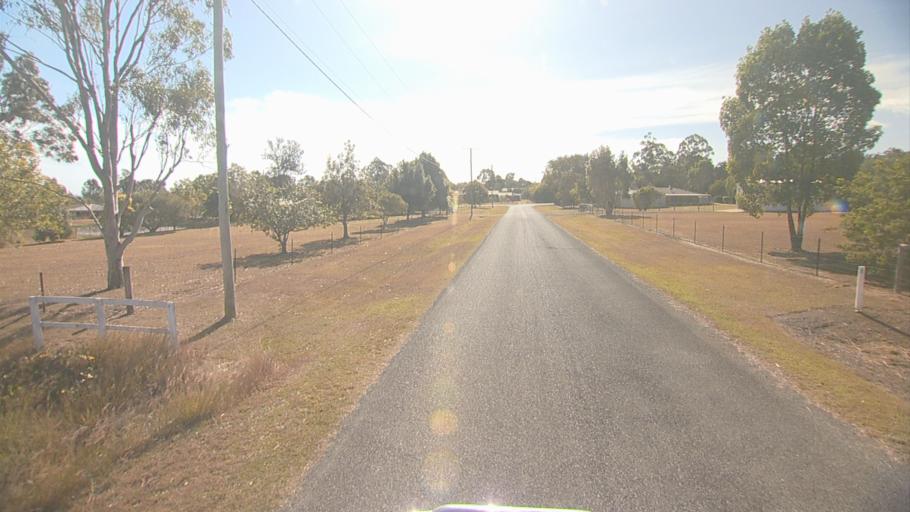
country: AU
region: Queensland
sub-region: Logan
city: Cedar Vale
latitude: -27.8694
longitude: 152.9686
